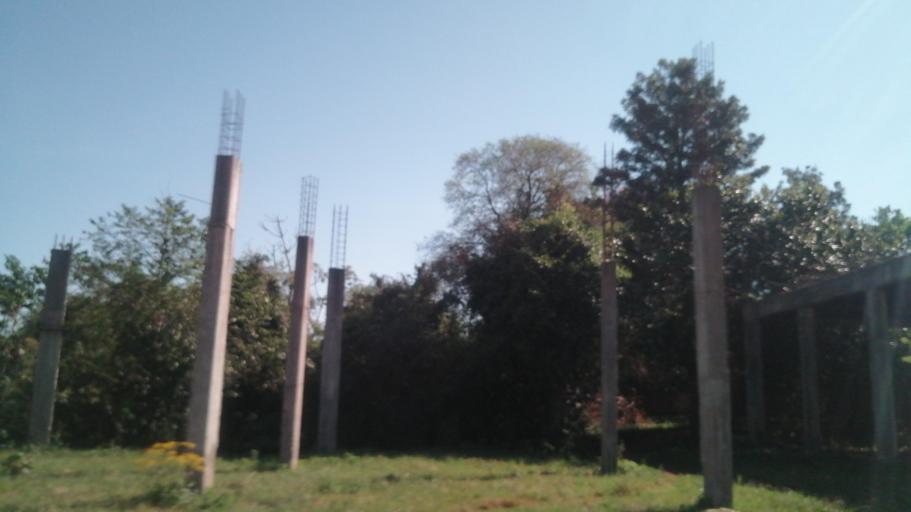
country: PY
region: Misiones
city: San Juan Bautista
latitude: -26.6747
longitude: -57.1337
